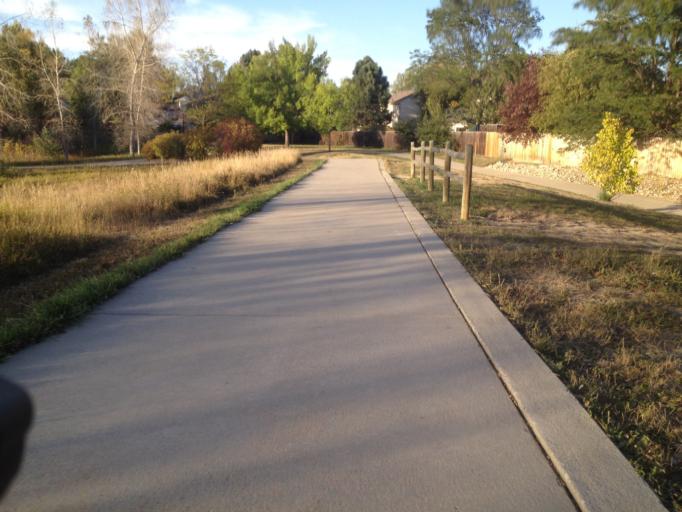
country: US
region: Colorado
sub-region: Boulder County
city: Louisville
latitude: 39.9833
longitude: -105.1423
